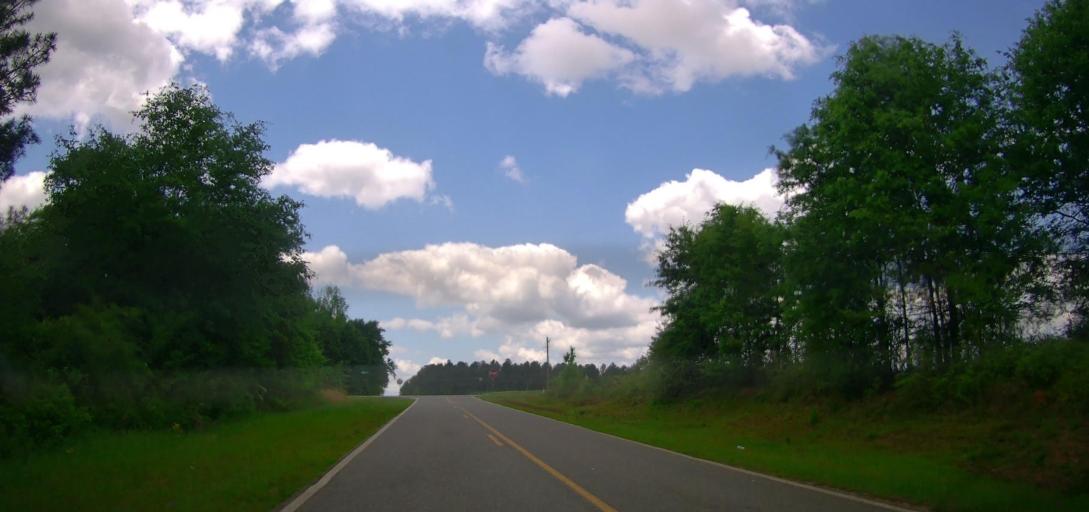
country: US
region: Georgia
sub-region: Laurens County
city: East Dublin
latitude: 32.6170
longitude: -82.8137
